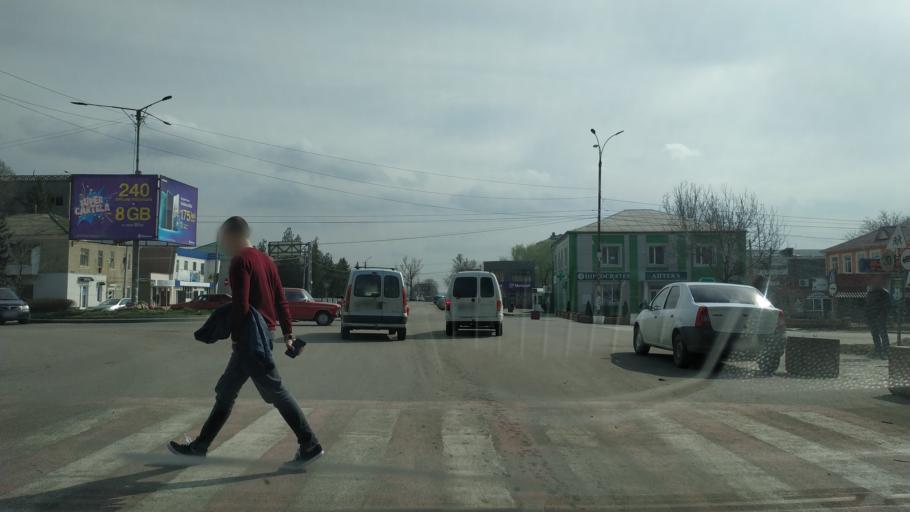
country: MD
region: Gagauzia
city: Vulcanesti
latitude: 45.6840
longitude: 28.4062
